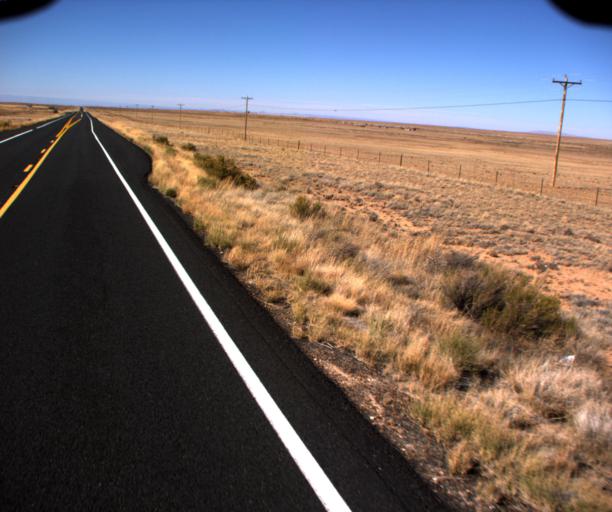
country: US
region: Arizona
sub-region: Coconino County
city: Tuba City
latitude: 35.9961
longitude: -111.0258
